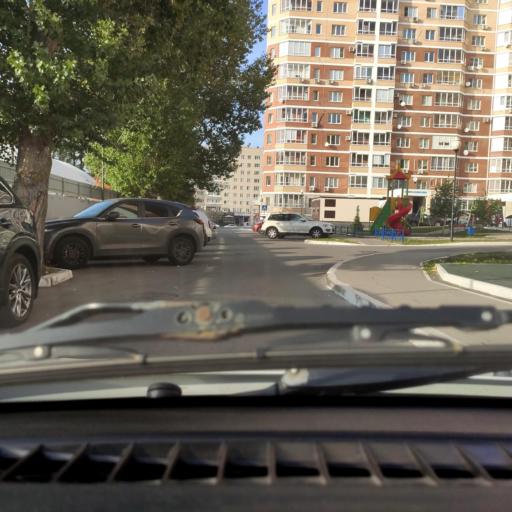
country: RU
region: Samara
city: Tol'yatti
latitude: 53.4994
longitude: 49.4205
